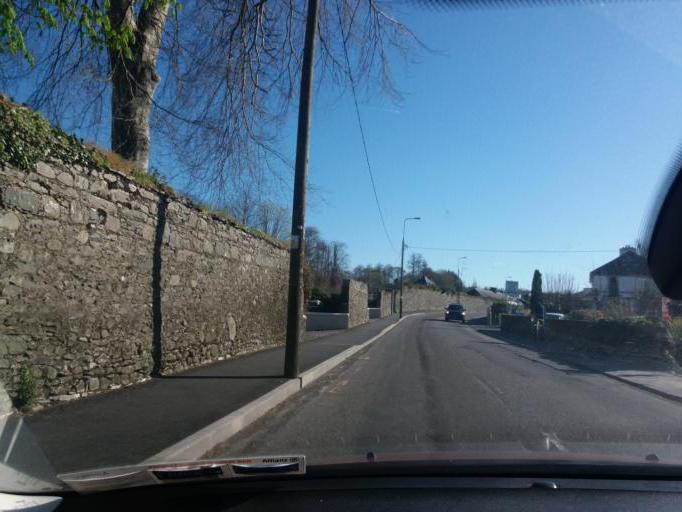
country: IE
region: Munster
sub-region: Ciarrai
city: Cill Airne
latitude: 52.0547
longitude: -9.5107
